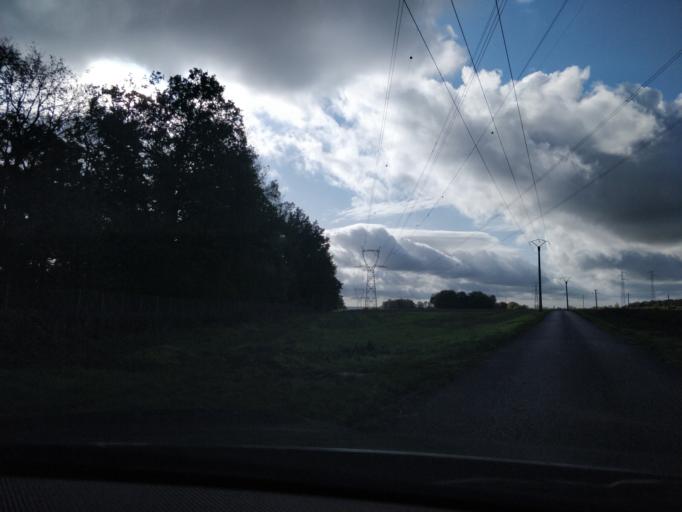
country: FR
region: Ile-de-France
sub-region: Departement de l'Essonne
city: Fontenay-les-Briis
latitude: 48.6313
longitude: 2.1498
